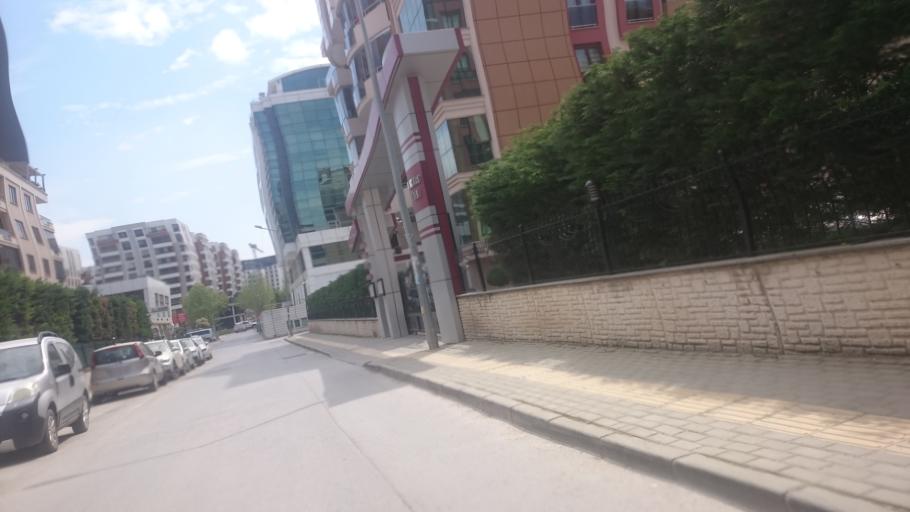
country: TR
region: Bursa
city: Cali
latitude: 40.2189
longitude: 28.9504
